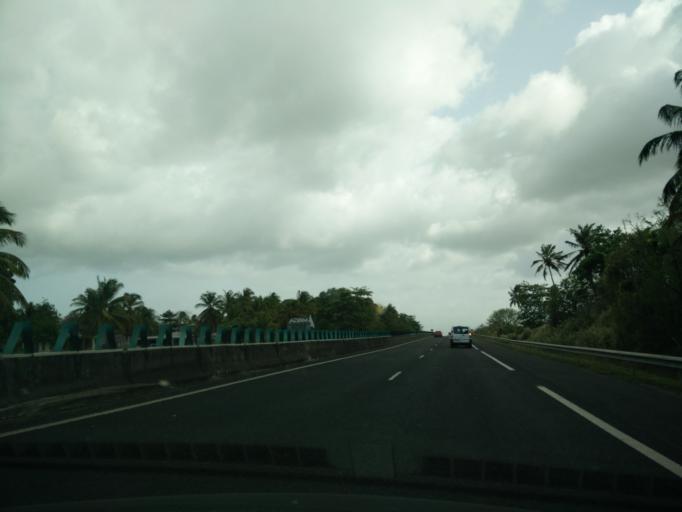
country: GP
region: Guadeloupe
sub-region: Guadeloupe
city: Les Abymes
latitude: 16.2838
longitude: -61.5063
